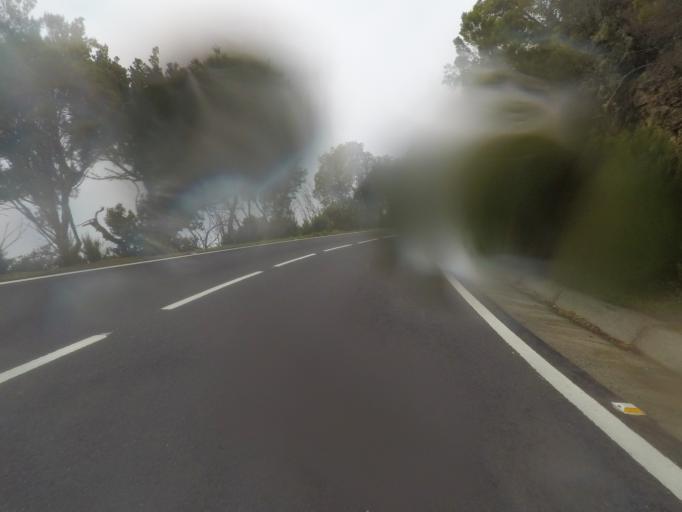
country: ES
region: Canary Islands
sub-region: Provincia de Santa Cruz de Tenerife
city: Vallehermosa
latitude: 28.1286
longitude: -17.2701
